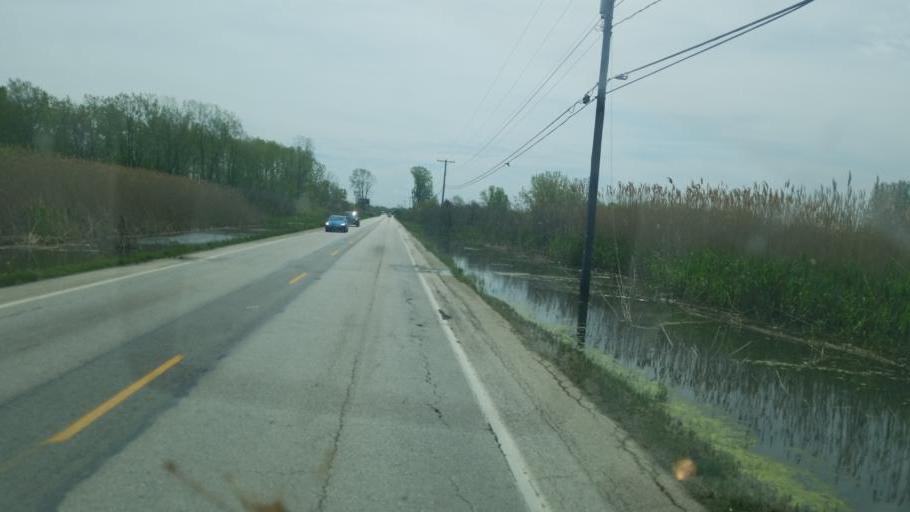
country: US
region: Ohio
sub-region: Ottawa County
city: Oak Harbor
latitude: 41.5726
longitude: -83.0853
